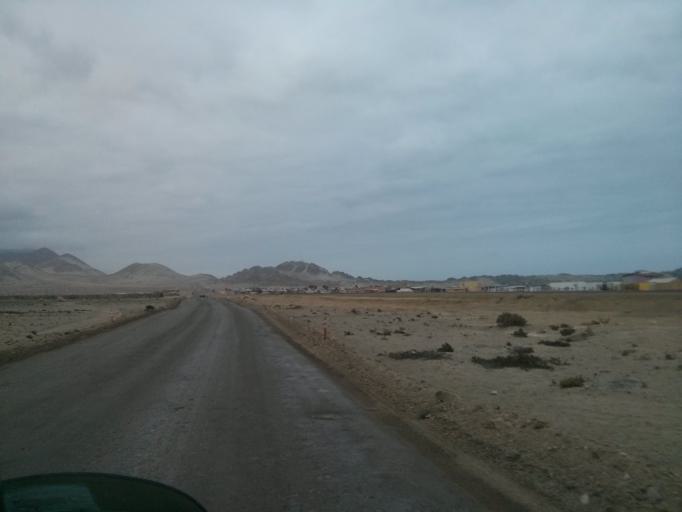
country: CL
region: Atacama
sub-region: Provincia de Chanaral
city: Diego de Almagro
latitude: -26.5634
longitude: -70.6776
